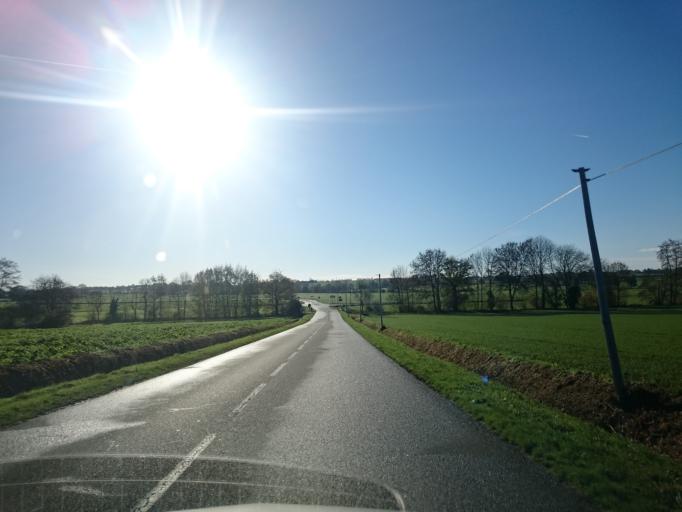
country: FR
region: Brittany
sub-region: Departement d'Ille-et-Vilaine
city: Corps-Nuds
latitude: 47.9504
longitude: -1.5672
